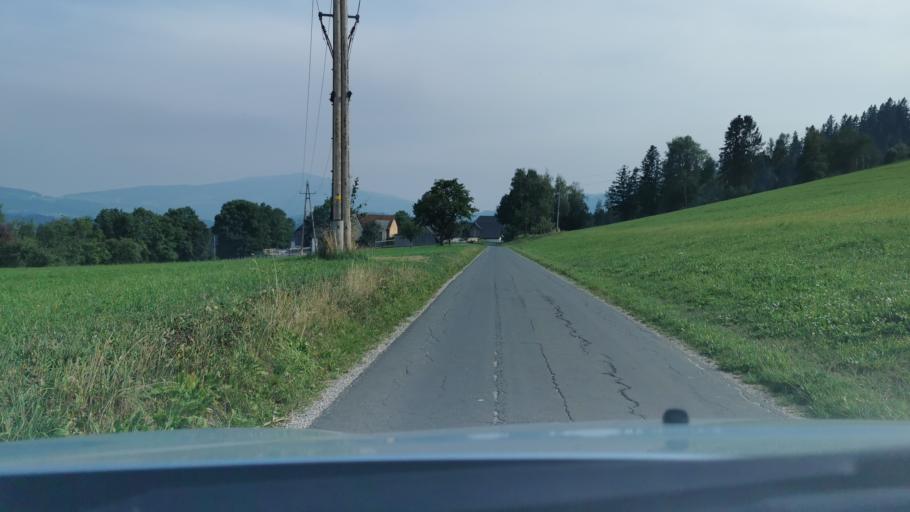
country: AT
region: Styria
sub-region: Politischer Bezirk Weiz
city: Fischbach
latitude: 47.3934
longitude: 15.6461
